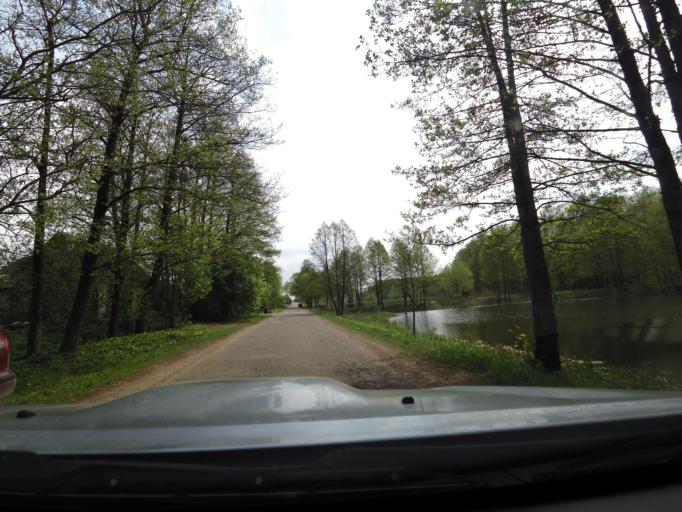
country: LT
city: Salcininkai
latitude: 54.4316
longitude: 25.3091
